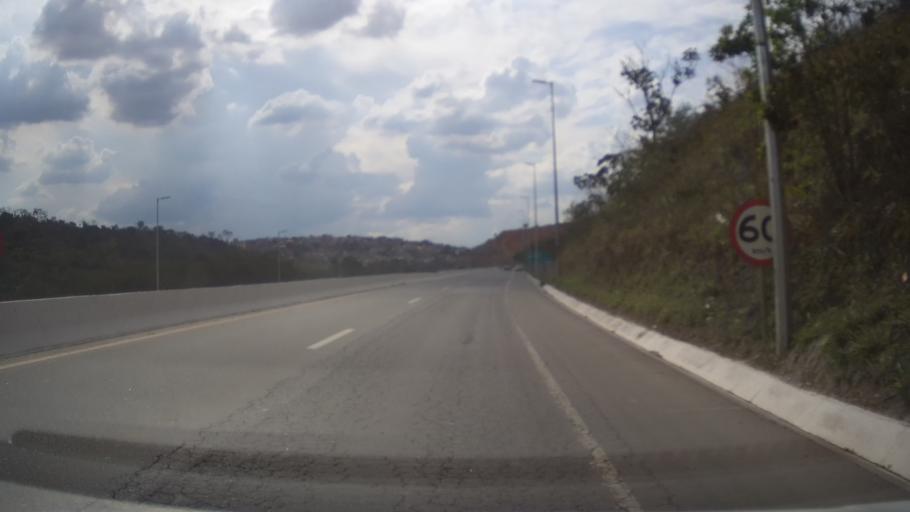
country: BR
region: Minas Gerais
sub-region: Belo Horizonte
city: Belo Horizonte
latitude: -19.8738
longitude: -43.8797
